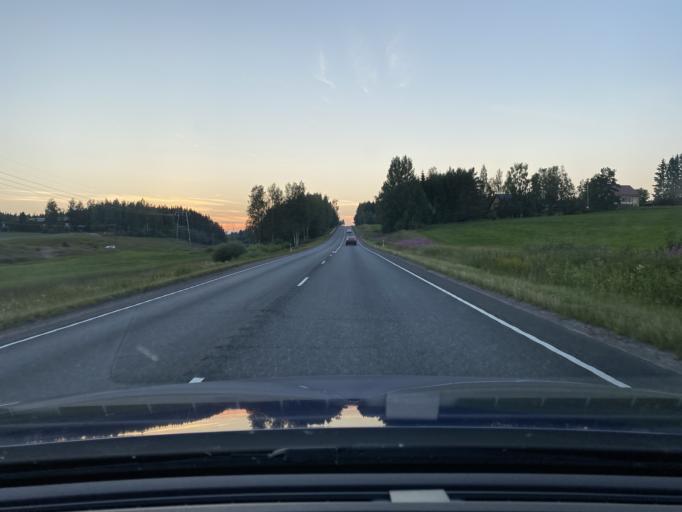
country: FI
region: Pirkanmaa
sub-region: Luoteis-Pirkanmaa
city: Ikaalinen
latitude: 61.8141
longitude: 22.9568
